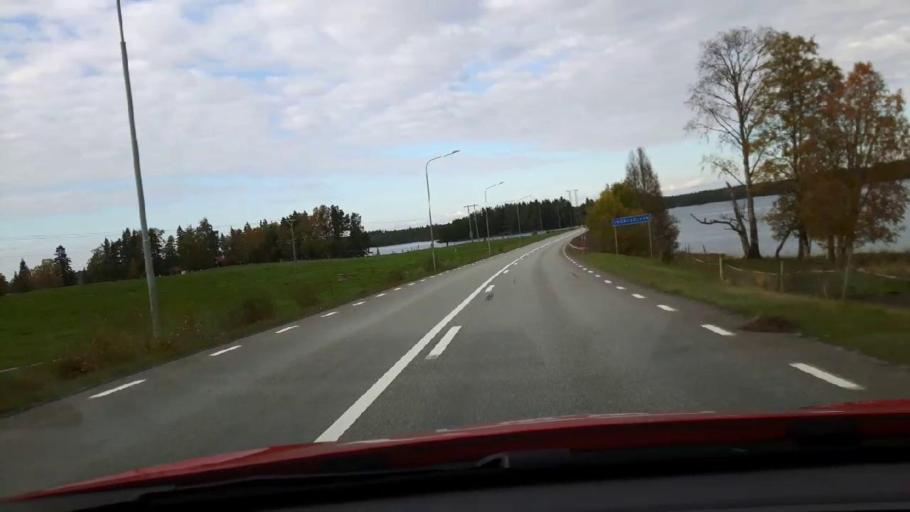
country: SE
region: Jaemtland
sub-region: Krokoms Kommun
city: Valla
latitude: 63.2434
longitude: 13.9996
